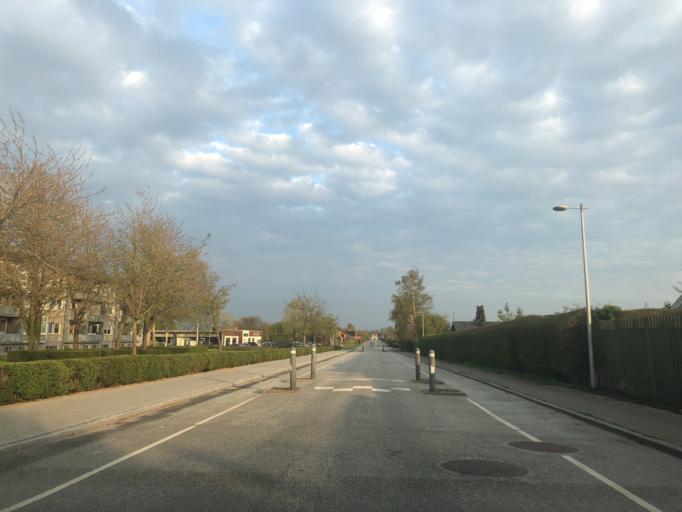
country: DK
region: Zealand
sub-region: Ringsted Kommune
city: Ringsted
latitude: 55.4632
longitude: 11.7881
